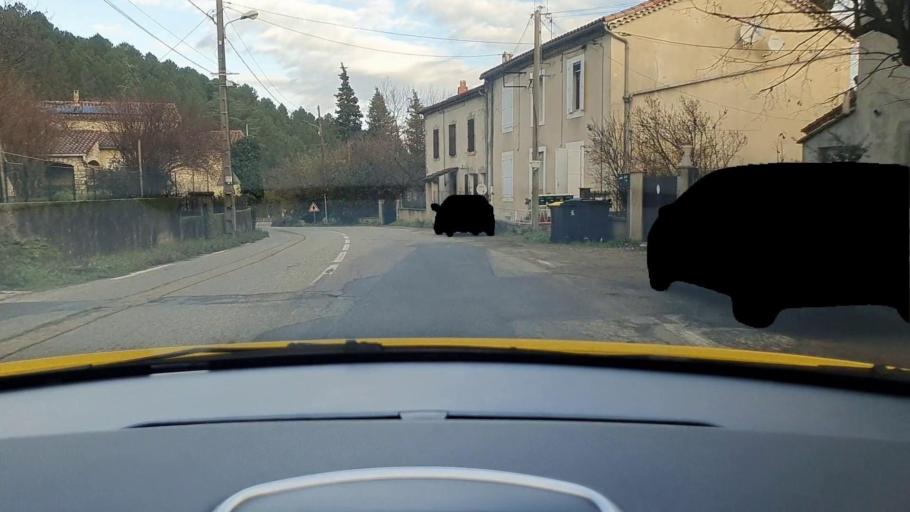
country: FR
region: Languedoc-Roussillon
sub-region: Departement du Gard
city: Laval-Pradel
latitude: 44.2345
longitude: 4.0562
